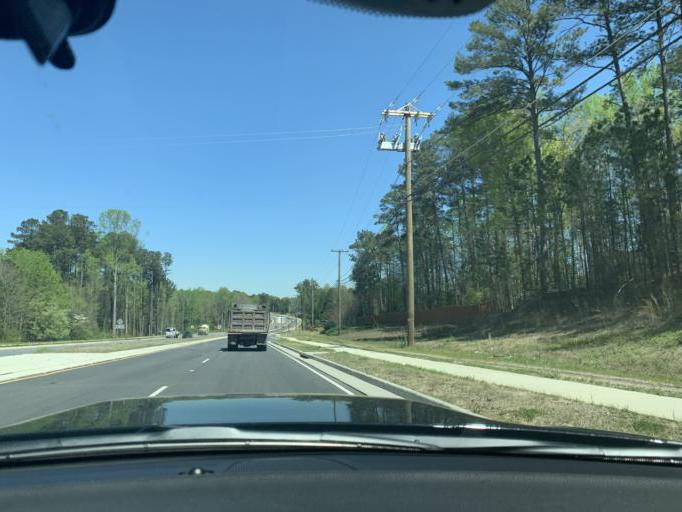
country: US
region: Georgia
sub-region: Forsyth County
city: Cumming
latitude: 34.2070
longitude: -84.1977
